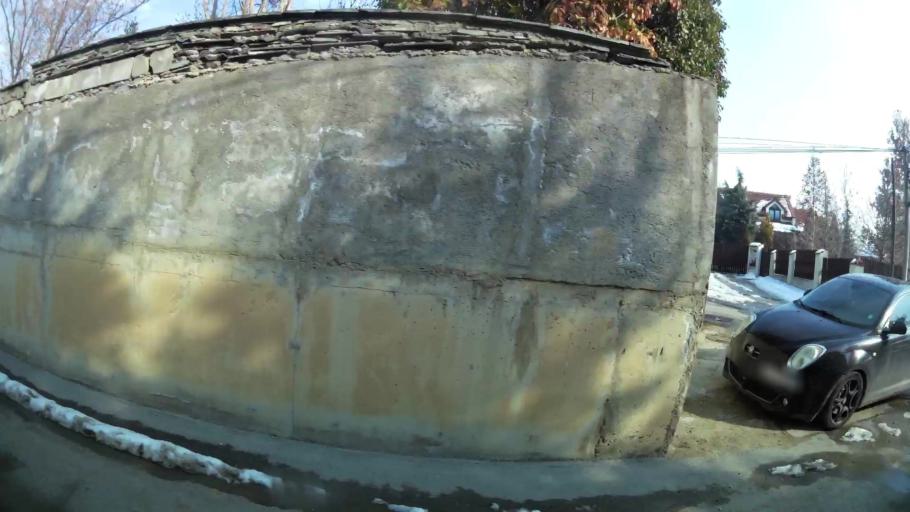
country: MK
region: Suto Orizari
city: Suto Orizare
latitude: 42.0306
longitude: 21.3771
